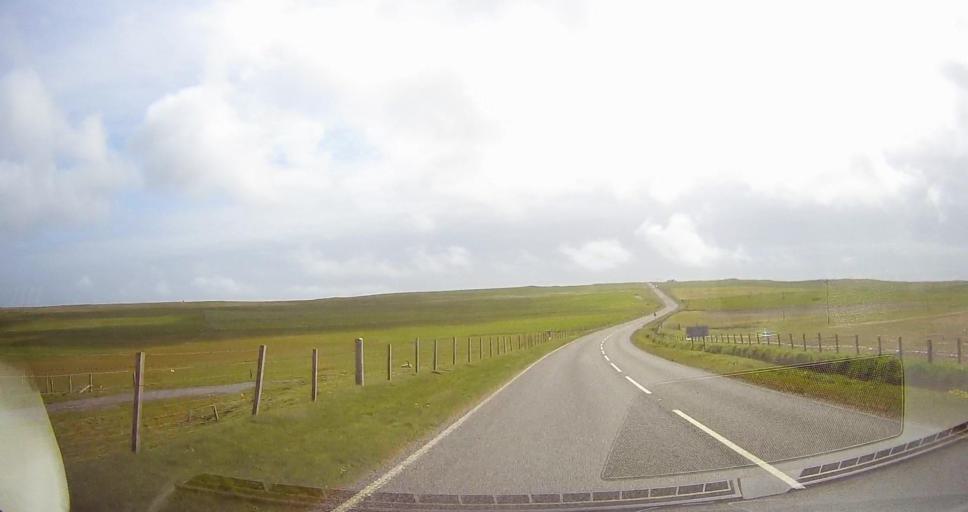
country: GB
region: Scotland
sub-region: Shetland Islands
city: Sandwick
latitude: 59.9102
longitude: -1.3012
